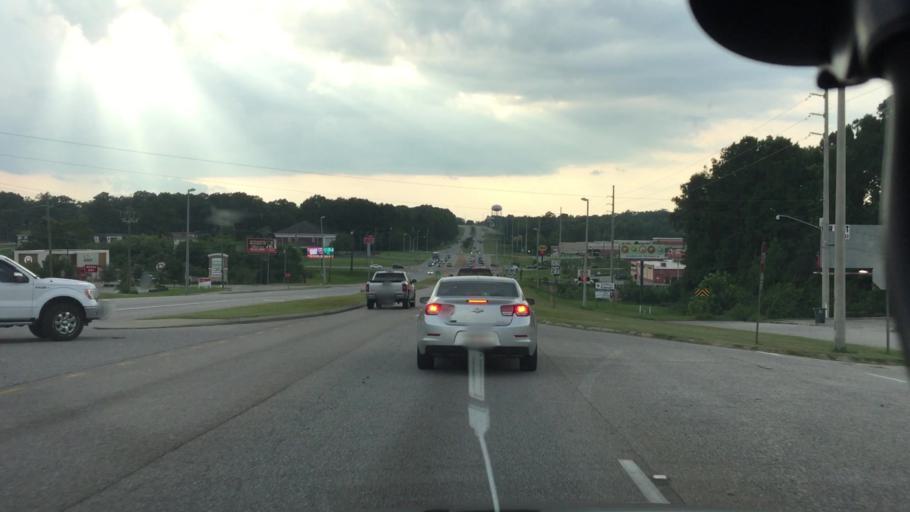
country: US
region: Alabama
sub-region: Coffee County
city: Enterprise
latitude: 31.3272
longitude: -85.8351
